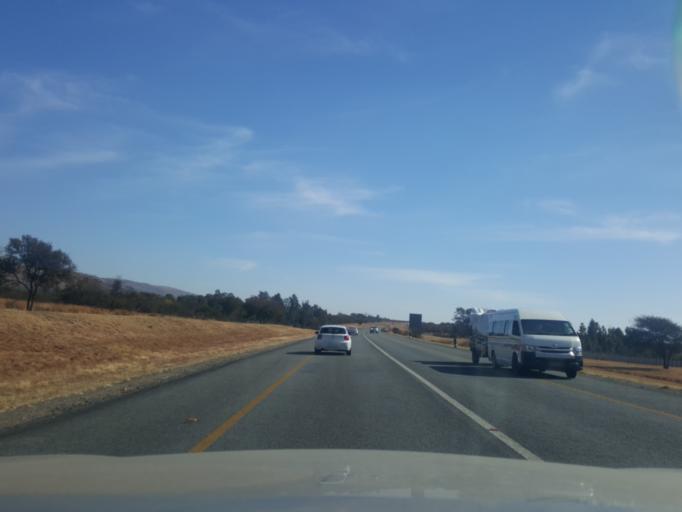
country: ZA
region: North-West
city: Ga-Rankuwa
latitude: -25.6571
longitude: 28.0297
